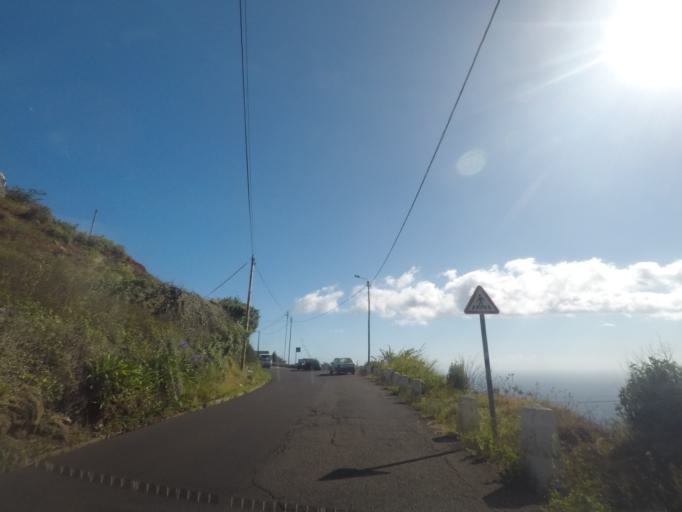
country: PT
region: Madeira
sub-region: Ribeira Brava
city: Campanario
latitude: 32.6646
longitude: -17.0206
